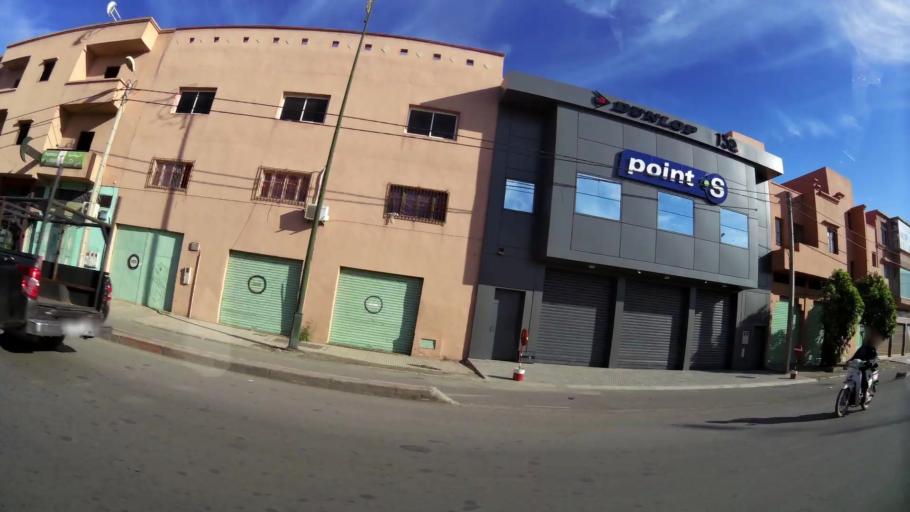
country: MA
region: Marrakech-Tensift-Al Haouz
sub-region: Marrakech
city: Marrakesh
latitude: 31.6809
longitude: -8.0508
